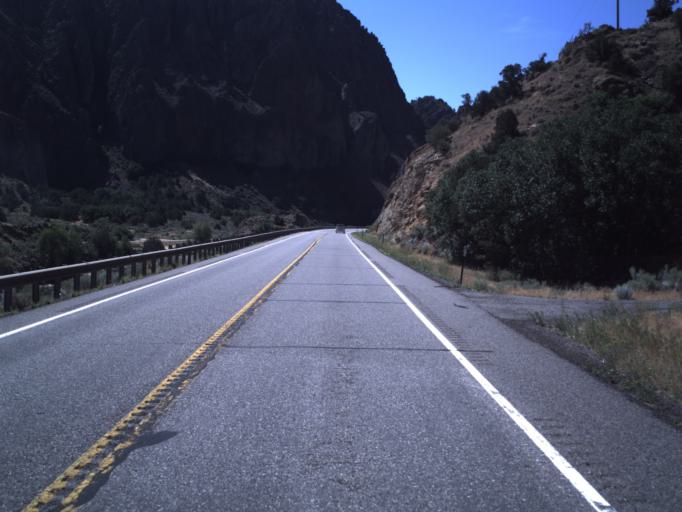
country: US
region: Utah
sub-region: Sevier County
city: Monroe
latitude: 38.5523
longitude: -112.2700
